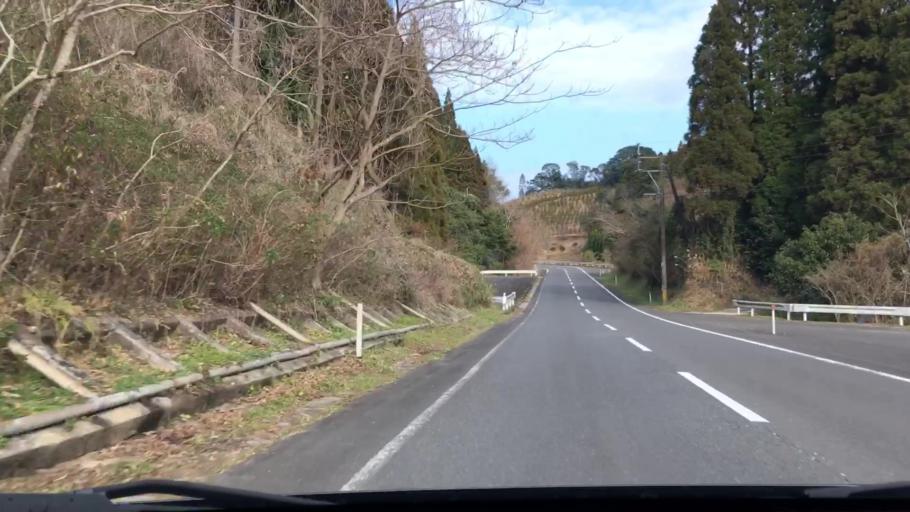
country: JP
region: Miyazaki
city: Kushima
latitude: 31.5708
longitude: 131.2626
